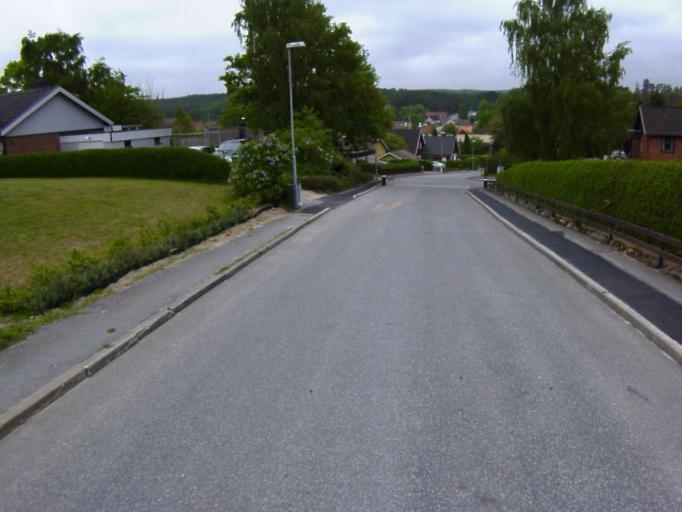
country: SE
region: Skane
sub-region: Kristianstads Kommun
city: Degeberga
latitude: 55.8395
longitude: 14.0887
